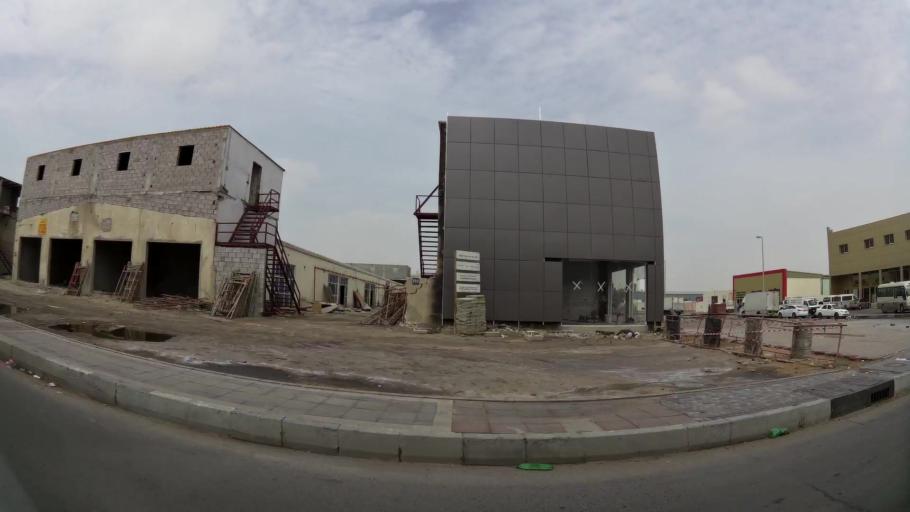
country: AE
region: Abu Dhabi
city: Abu Dhabi
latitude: 24.3544
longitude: 54.4903
